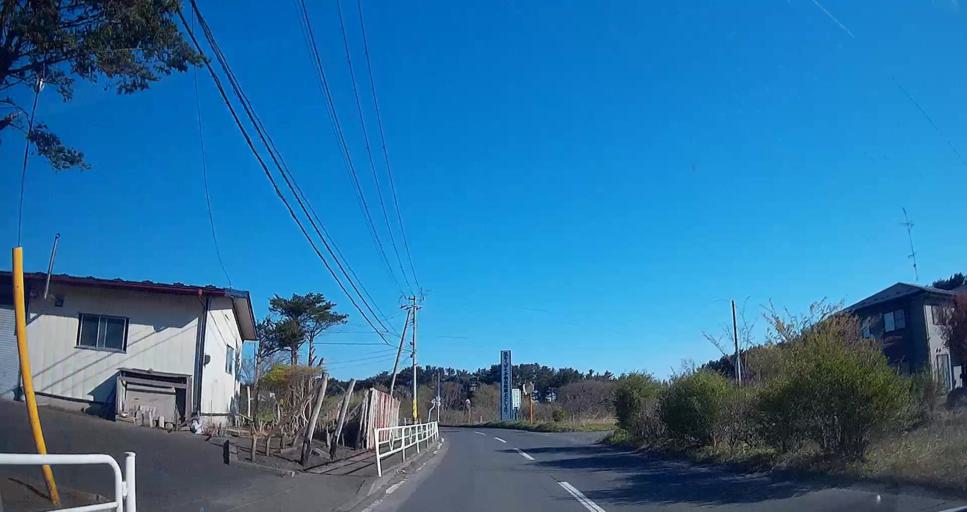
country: JP
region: Aomori
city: Hachinohe
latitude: 40.5119
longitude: 141.6068
